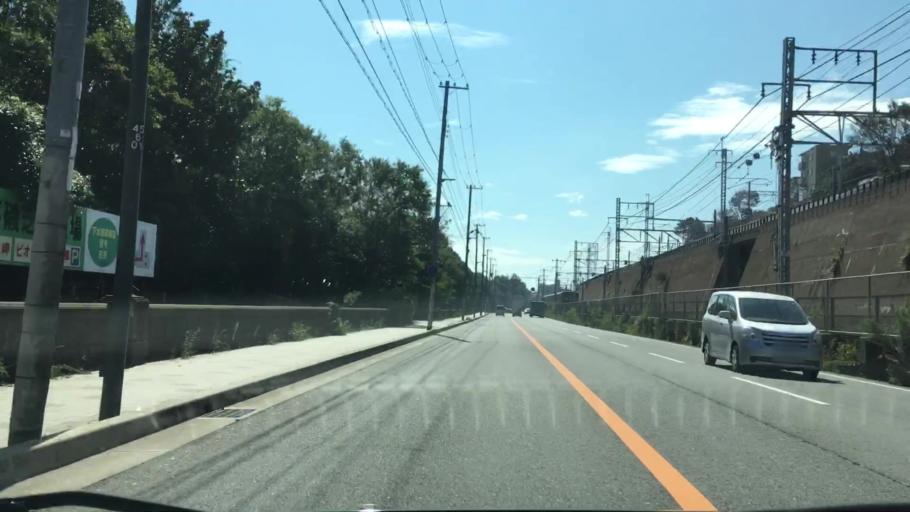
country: JP
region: Hyogo
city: Akashi
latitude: 34.6301
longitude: 135.0703
